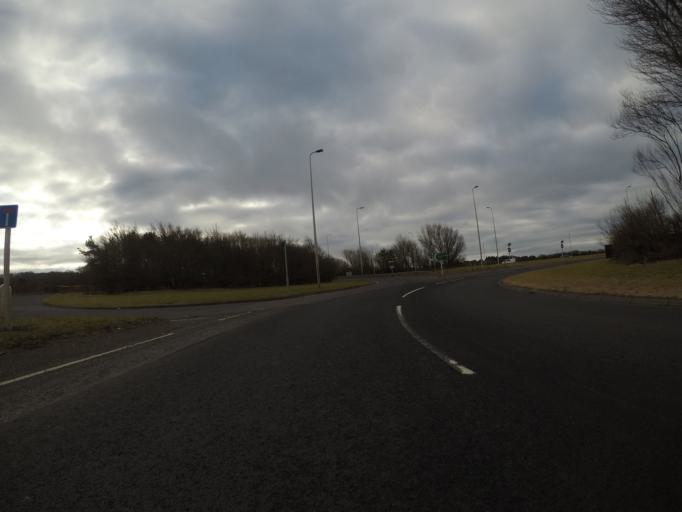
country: GB
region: Scotland
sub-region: North Ayrshire
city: Dreghorn
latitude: 55.5762
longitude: -4.6408
